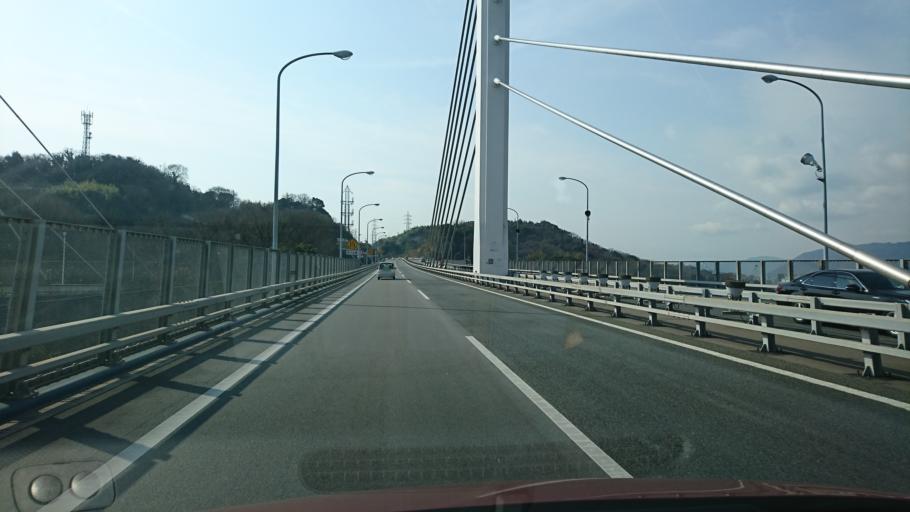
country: JP
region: Hiroshima
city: Onomichi
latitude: 34.4093
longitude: 133.2159
